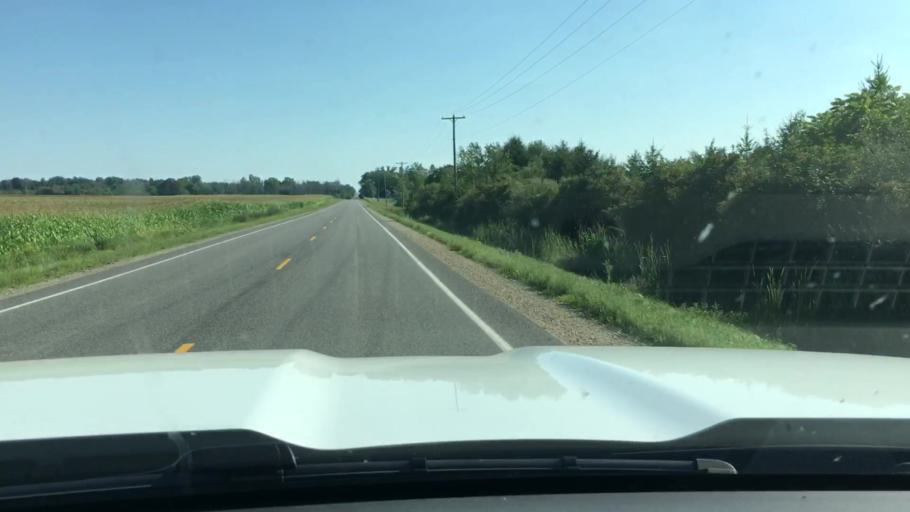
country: US
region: Michigan
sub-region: Muskegon County
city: Ravenna
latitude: 43.1530
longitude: -85.9278
